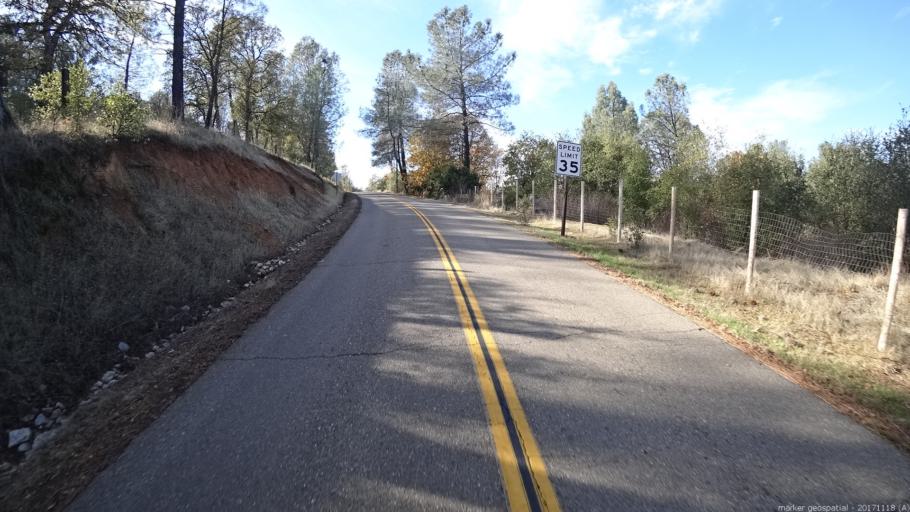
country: US
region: California
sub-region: Shasta County
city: Anderson
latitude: 40.4727
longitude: -122.3992
